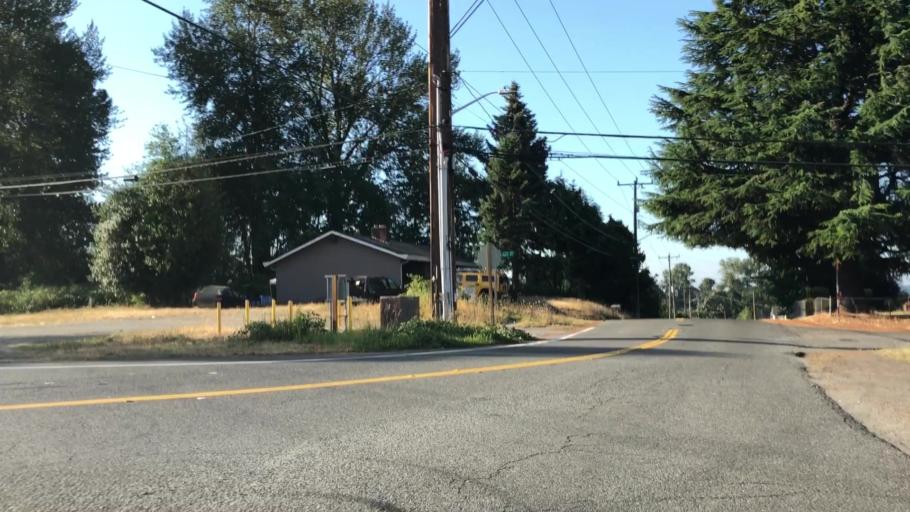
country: US
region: Washington
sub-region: King County
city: Bryn Mawr-Skyway
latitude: 47.4960
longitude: -122.2596
